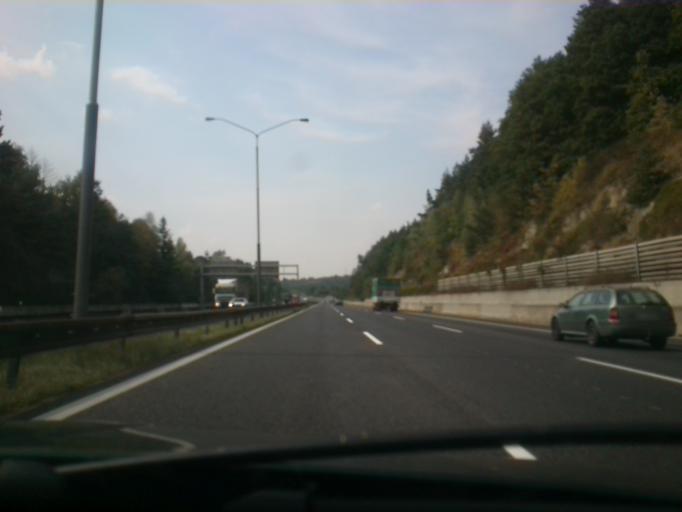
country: CZ
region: Central Bohemia
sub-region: Okres Praha-Vychod
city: Mnichovice
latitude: 49.9206
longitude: 14.7054
